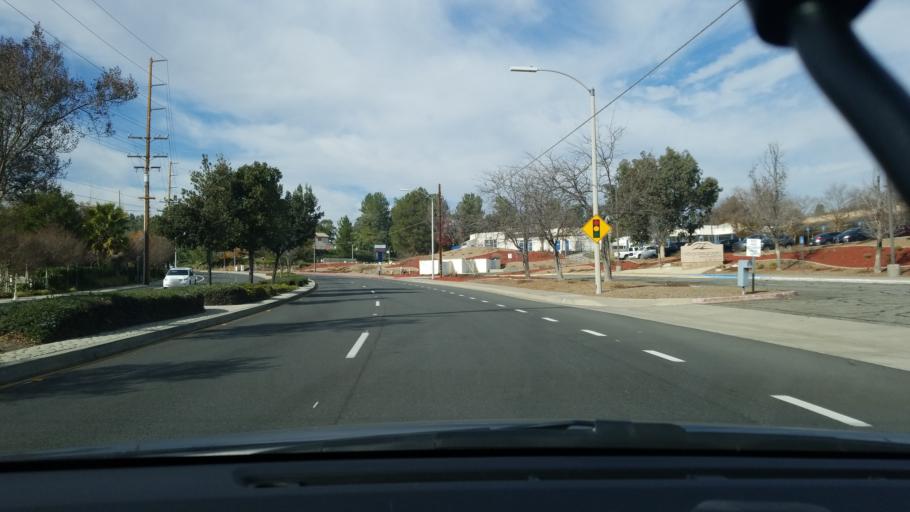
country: US
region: California
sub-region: Riverside County
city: Temecula
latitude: 33.4862
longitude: -117.1037
